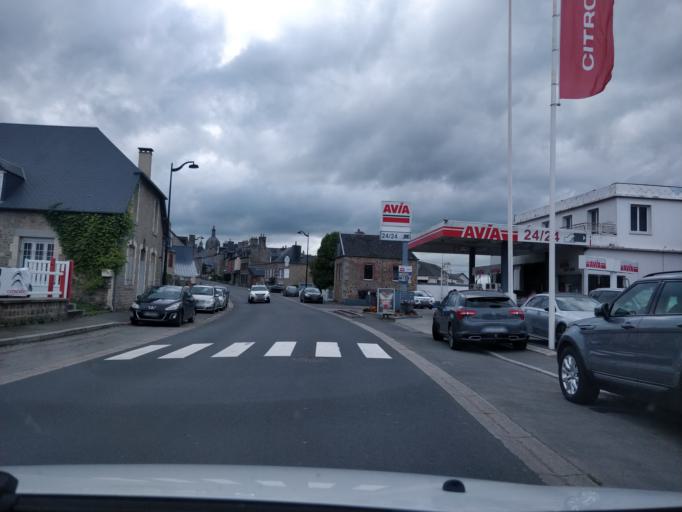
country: FR
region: Lower Normandy
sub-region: Departement du Calvados
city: Saint-Sever-Calvados
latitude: 48.8404
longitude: -1.0429
